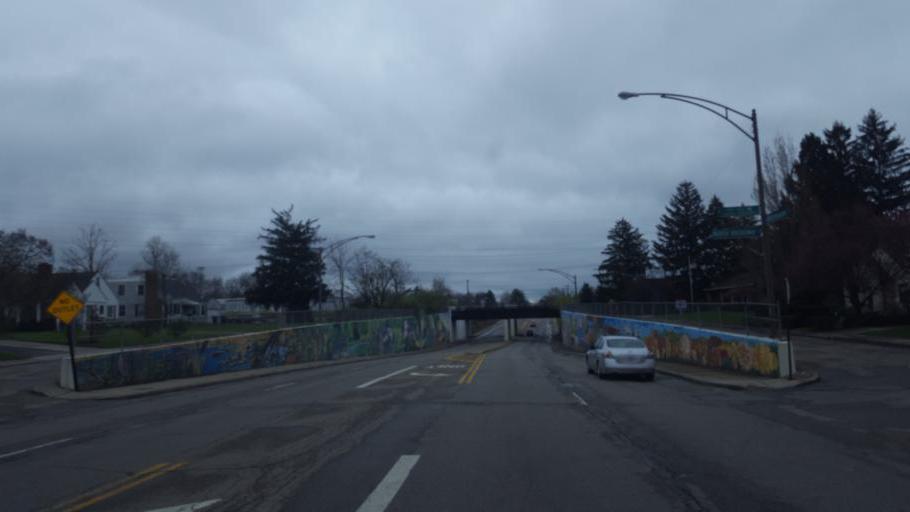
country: US
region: Ohio
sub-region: Franklin County
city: Worthington
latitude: 40.0313
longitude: -82.9994
